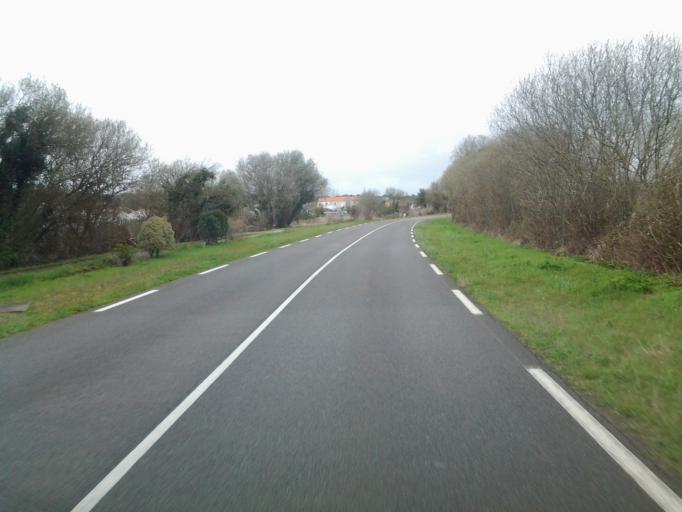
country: FR
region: Pays de la Loire
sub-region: Departement de la Vendee
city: La Tranche-sur-Mer
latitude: 46.3645
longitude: -1.4555
